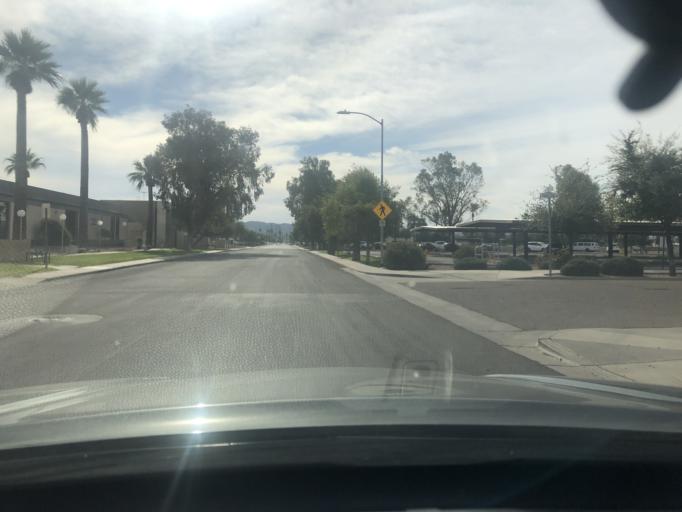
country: US
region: Arizona
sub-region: Maricopa County
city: Phoenix
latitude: 33.4540
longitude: -112.0433
